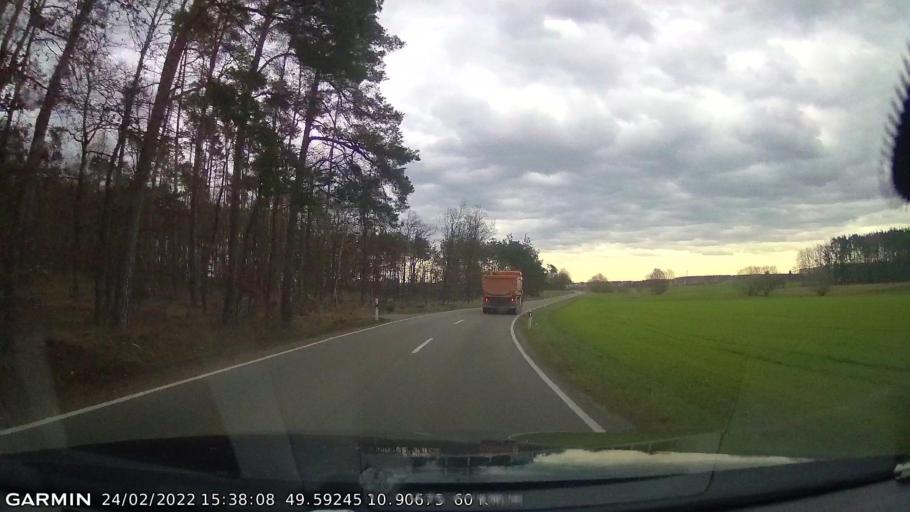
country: DE
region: Bavaria
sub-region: Regierungsbezirk Mittelfranken
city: Herzogenaurach
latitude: 49.5925
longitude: 10.9067
